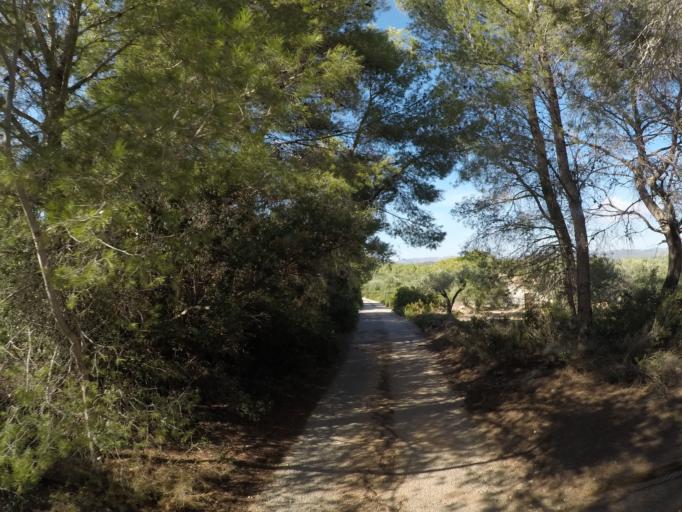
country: ES
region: Catalonia
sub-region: Provincia de Tarragona
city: El Perello
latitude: 40.9169
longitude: 0.7236
